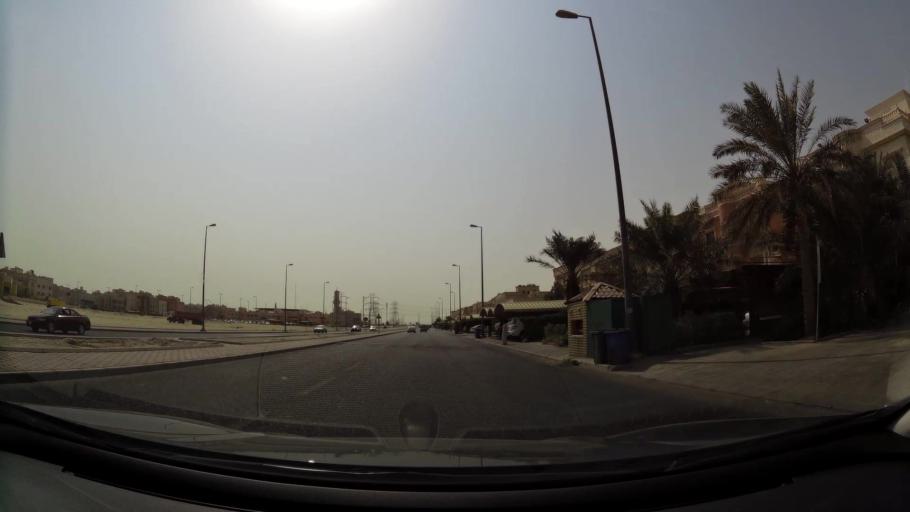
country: KW
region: Muhafazat al Jahra'
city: Al Jahra'
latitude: 29.3046
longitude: 47.7238
